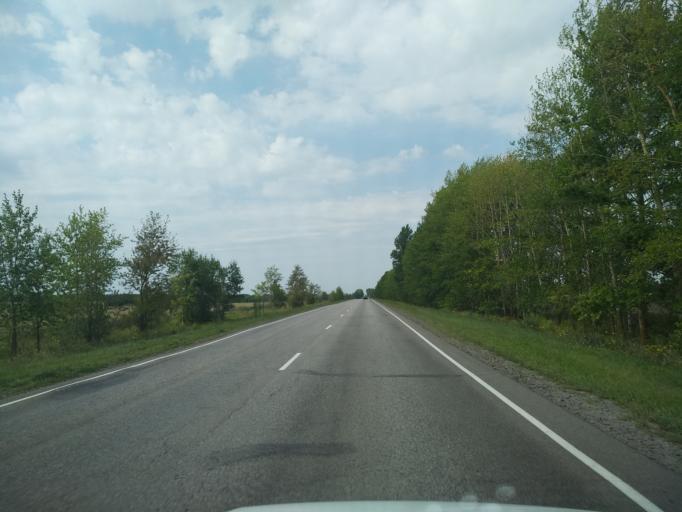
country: RU
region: Voronezj
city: Pereleshino
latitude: 51.7169
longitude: 40.0174
